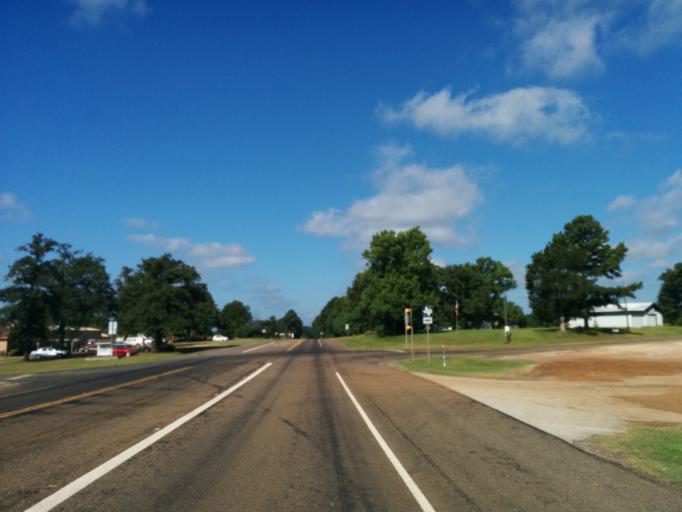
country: US
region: Texas
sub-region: Sabine County
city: Milam
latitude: 31.4202
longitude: -93.9748
